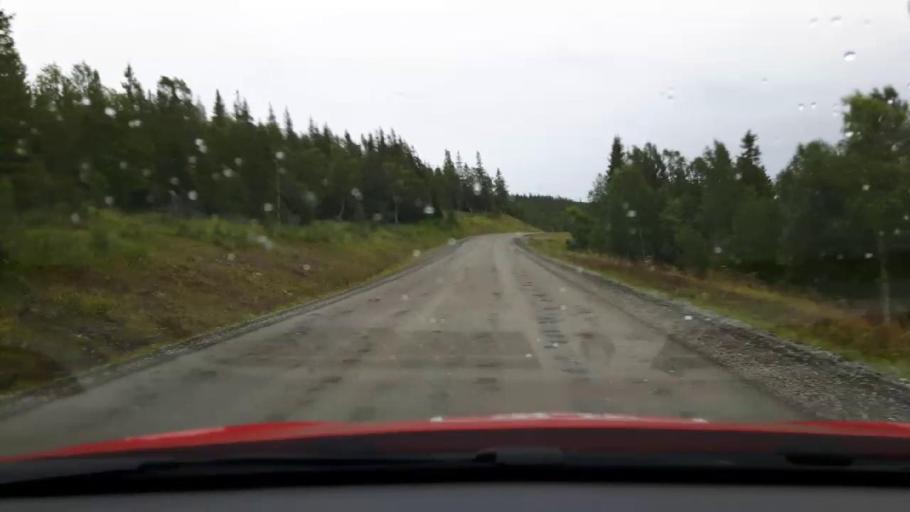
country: NO
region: Nord-Trondelag
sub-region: Meraker
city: Meraker
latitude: 63.5497
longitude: 12.3748
